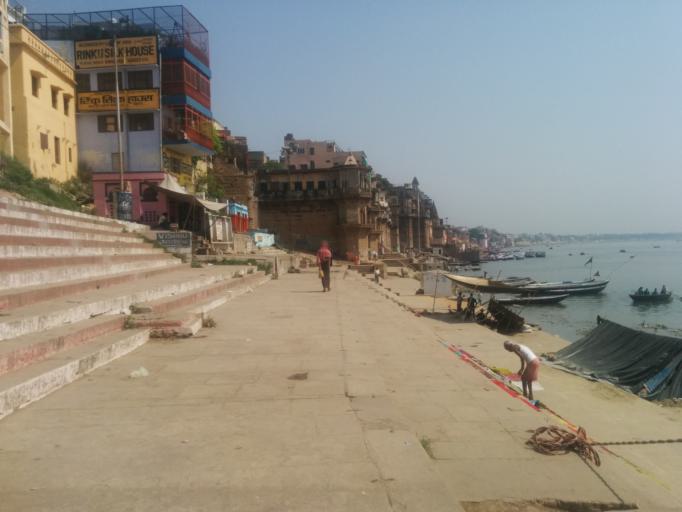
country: IN
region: Uttar Pradesh
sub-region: Varanasi
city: Varanasi
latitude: 25.3034
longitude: 83.0083
